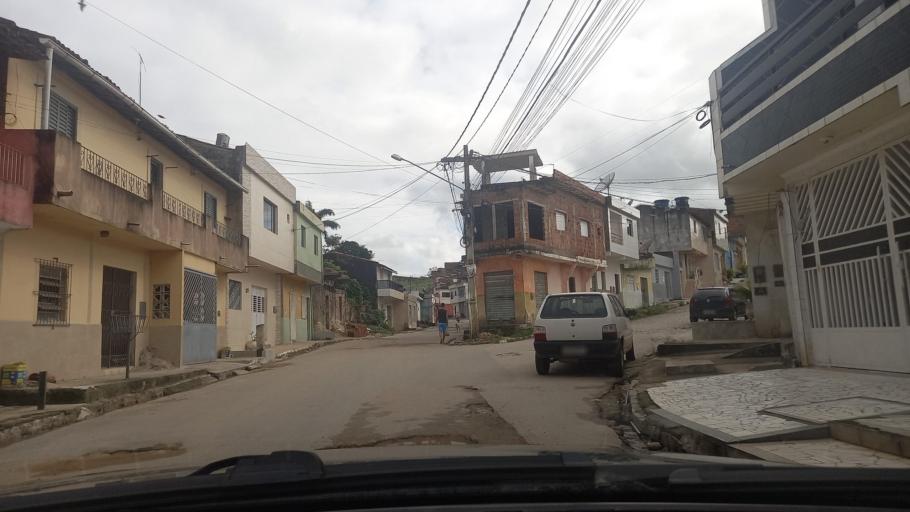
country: BR
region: Pernambuco
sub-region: Vitoria De Santo Antao
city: Vitoria de Santo Antao
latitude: -8.1124
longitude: -35.3008
